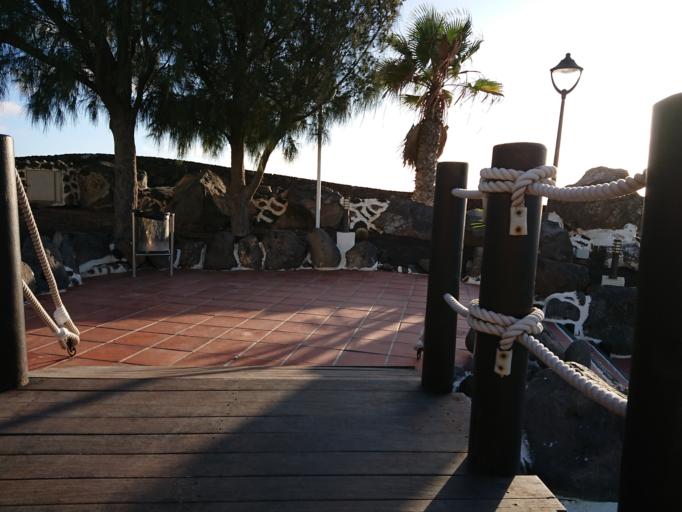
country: ES
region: Canary Islands
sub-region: Provincia de Las Palmas
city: Playa Blanca
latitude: 28.8593
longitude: -13.8447
